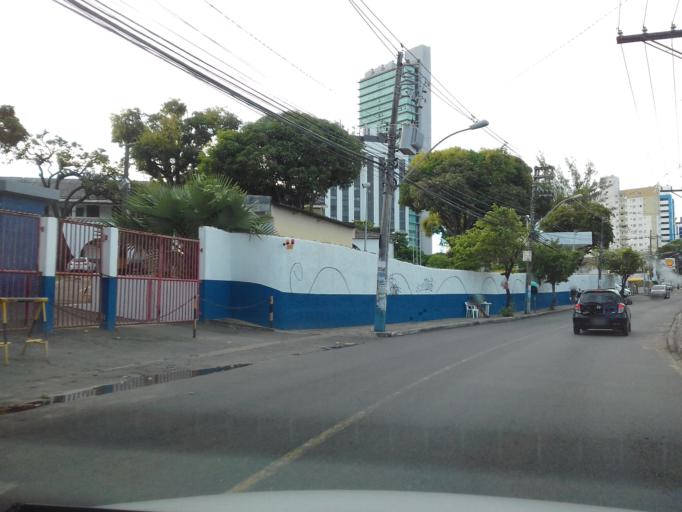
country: BR
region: Bahia
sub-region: Salvador
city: Salvador
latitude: -13.0035
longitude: -38.5004
